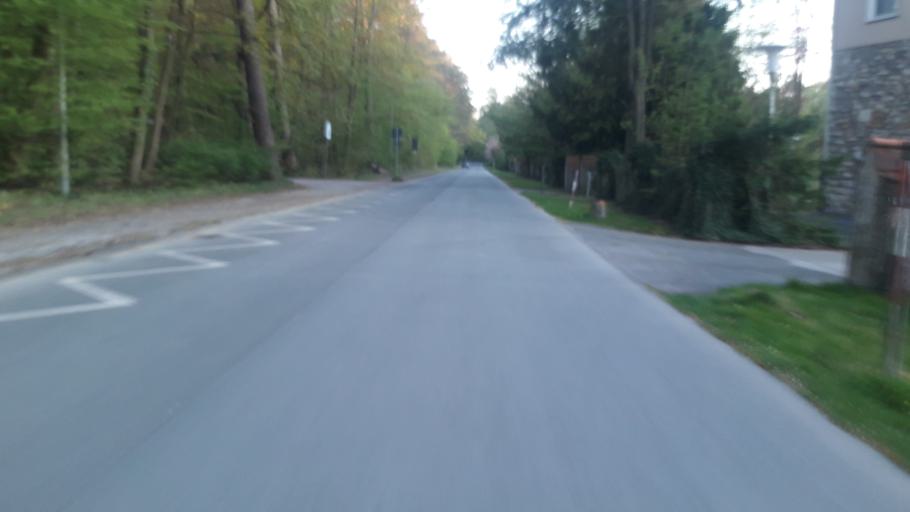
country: DE
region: North Rhine-Westphalia
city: Bad Lippspringe
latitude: 51.7888
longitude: 8.8050
